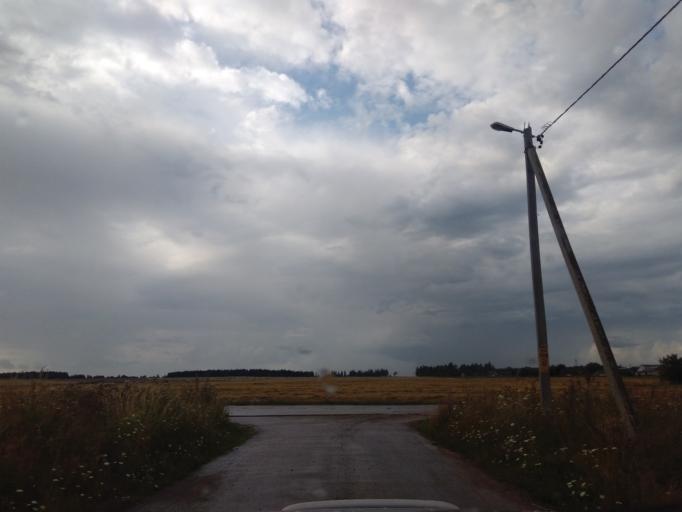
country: BY
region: Minsk
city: Kapyl'
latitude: 53.1673
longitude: 27.0791
